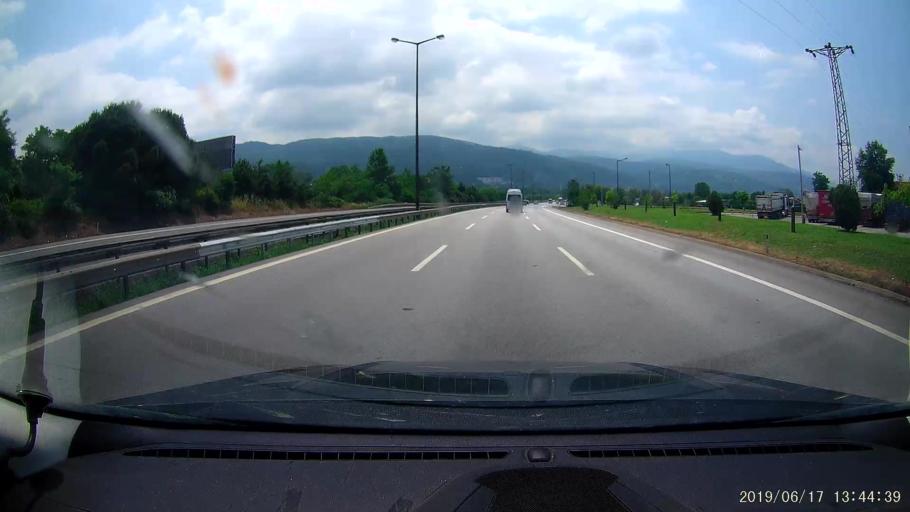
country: TR
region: Sakarya
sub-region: Merkez
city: Sapanca
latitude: 40.6917
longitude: 30.2834
